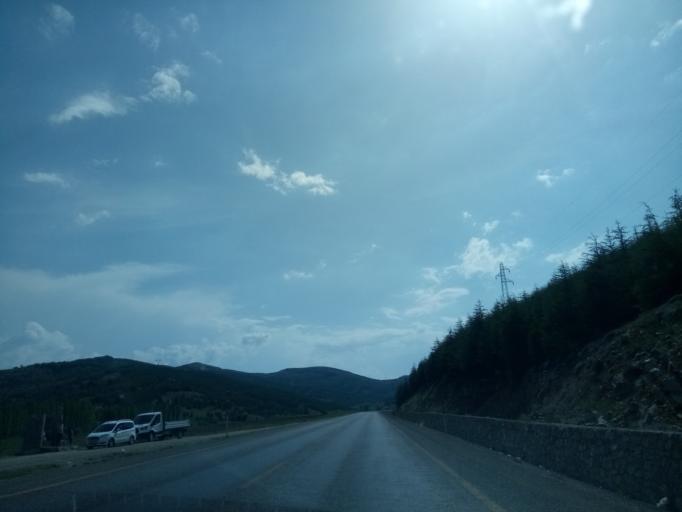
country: TR
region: Konya
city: Aksehir
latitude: 38.2558
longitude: 31.3766
